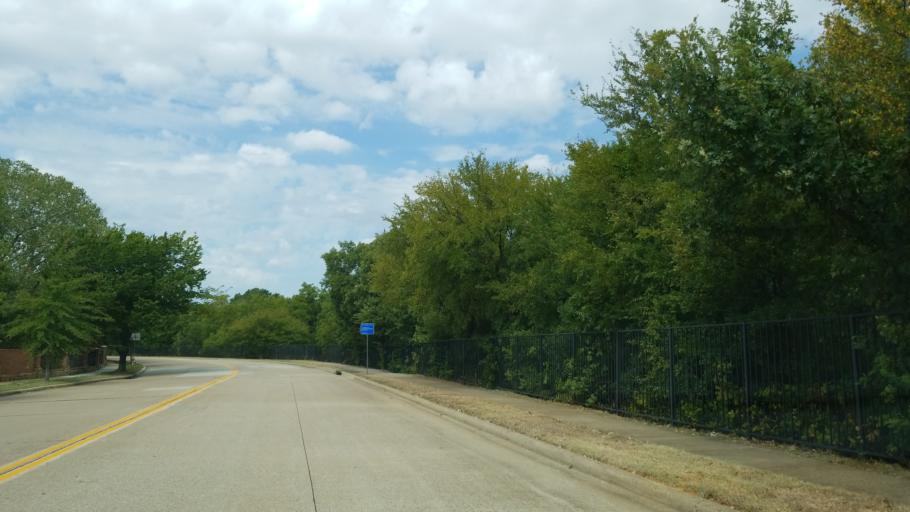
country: US
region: Texas
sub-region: Tarrant County
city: Grapevine
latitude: 32.9008
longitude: -97.1026
